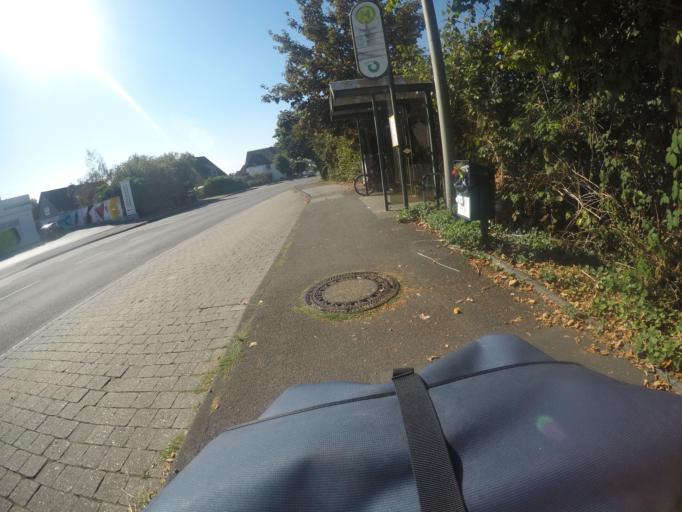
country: DE
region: North Rhine-Westphalia
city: Leichlingen
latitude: 51.0941
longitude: 6.9977
